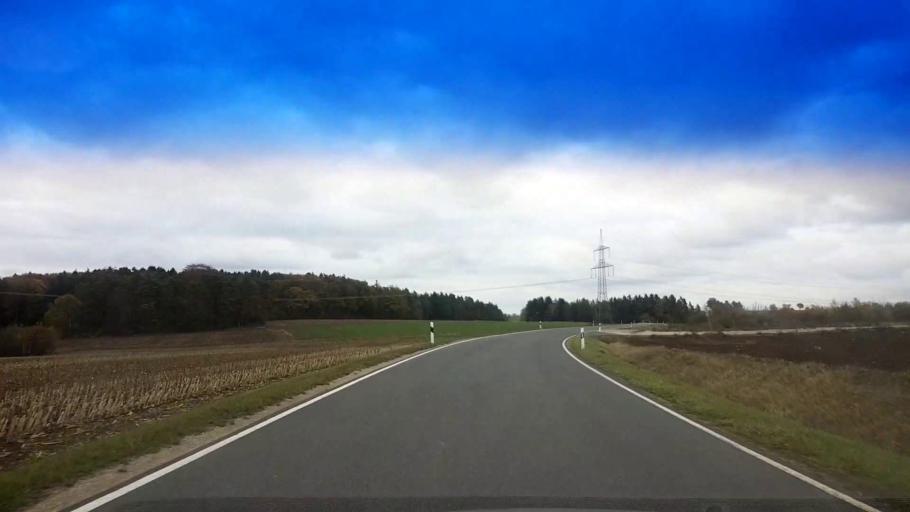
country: DE
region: Bavaria
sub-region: Upper Franconia
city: Poxdorf
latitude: 49.9454
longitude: 11.1007
